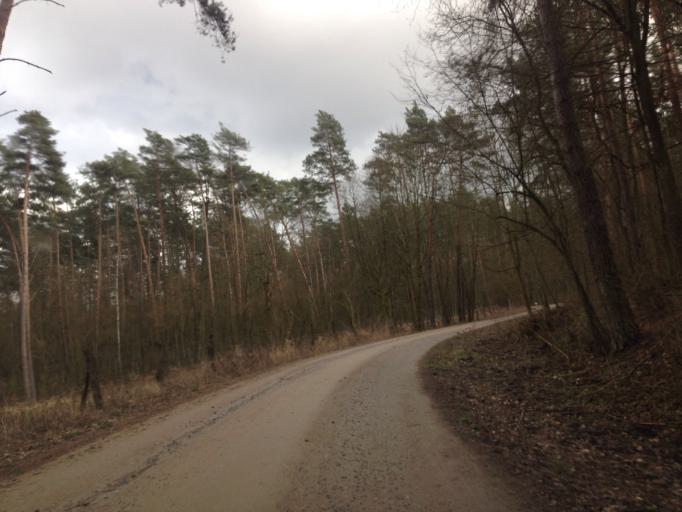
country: PL
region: Kujawsko-Pomorskie
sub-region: Powiat brodnicki
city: Gorzno
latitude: 53.2248
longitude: 19.6671
